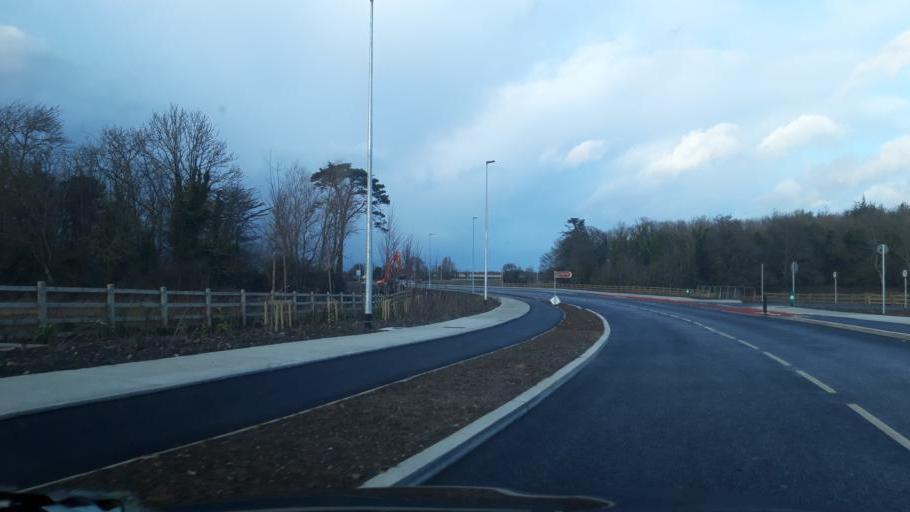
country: IE
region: Leinster
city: Donabate
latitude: 53.4894
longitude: -6.1313
